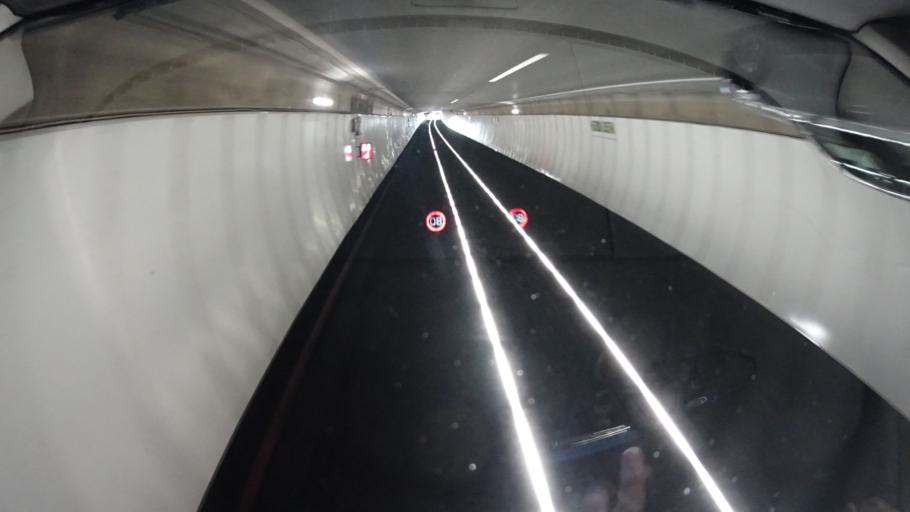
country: ES
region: Basque Country
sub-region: Bizkaia
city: Basauri
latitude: 43.2332
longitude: -2.9038
